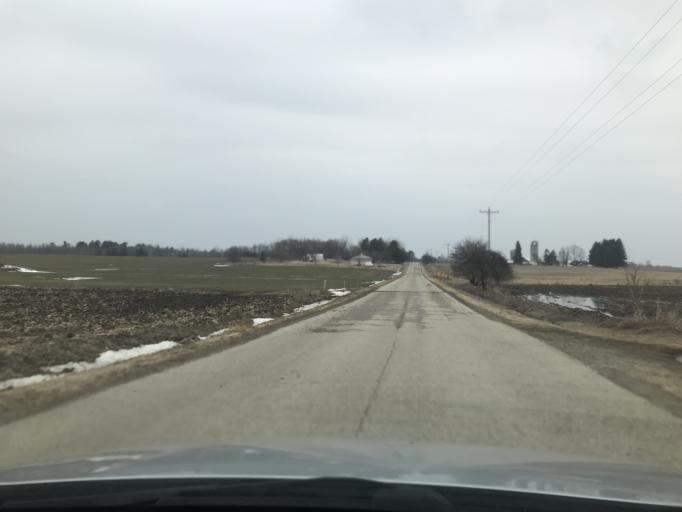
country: US
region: Wisconsin
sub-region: Marinette County
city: Peshtigo
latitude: 45.0591
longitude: -87.8509
